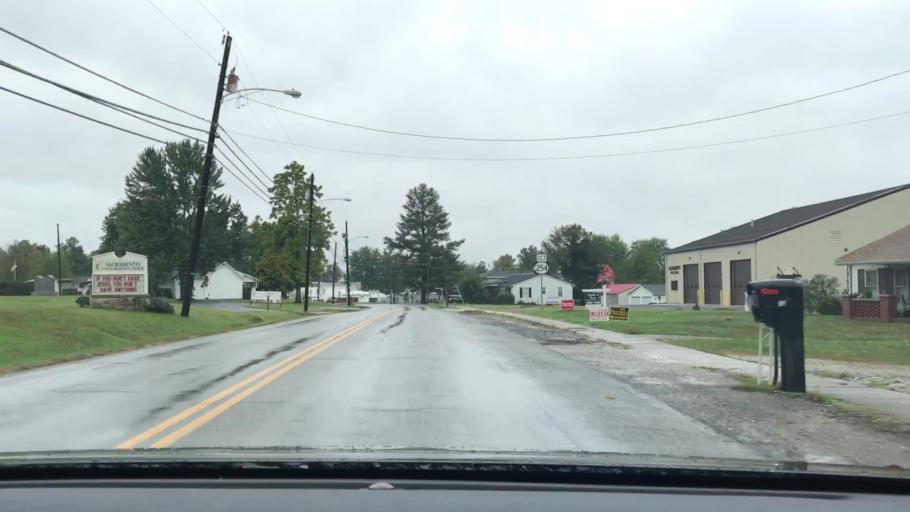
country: US
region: Kentucky
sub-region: McLean County
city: Calhoun
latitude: 37.4189
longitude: -87.2660
